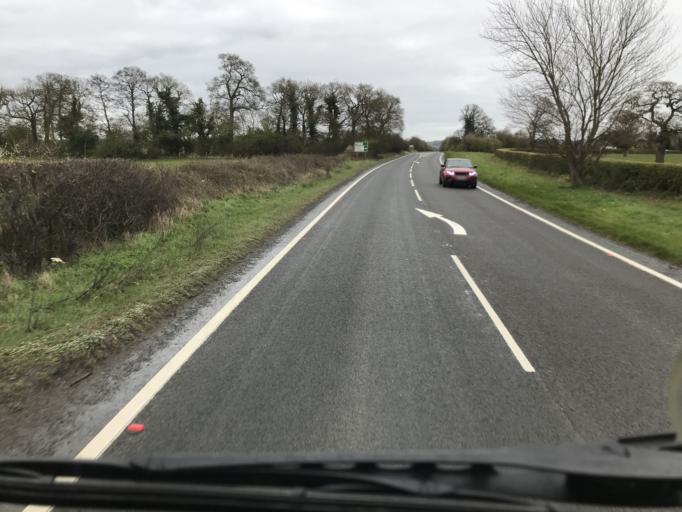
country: GB
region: England
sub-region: Cheshire West and Chester
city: Tattenhall
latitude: 53.1195
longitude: -2.8015
